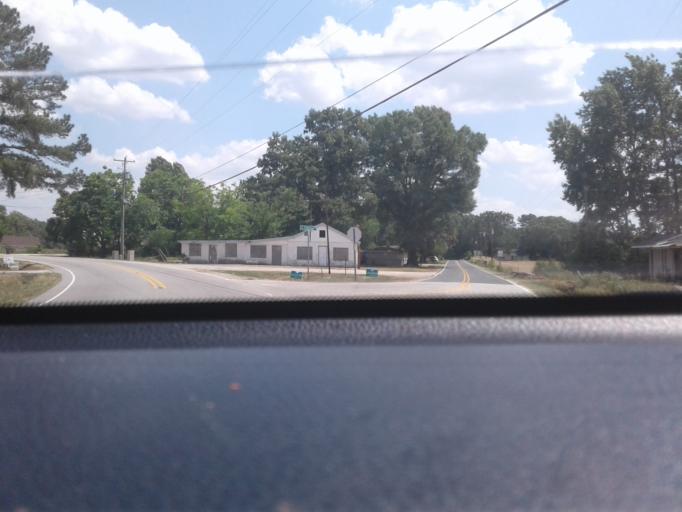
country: US
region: North Carolina
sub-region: Harnett County
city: Erwin
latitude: 35.3146
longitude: -78.6803
